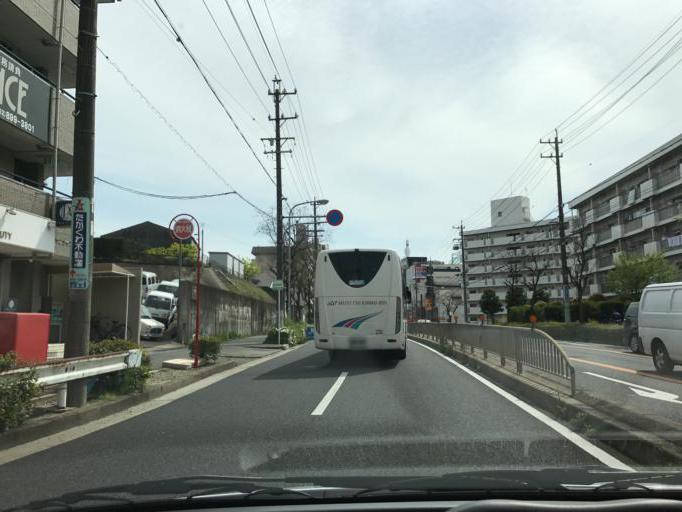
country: JP
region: Aichi
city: Nagoya-shi
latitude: 35.1006
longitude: 136.9545
